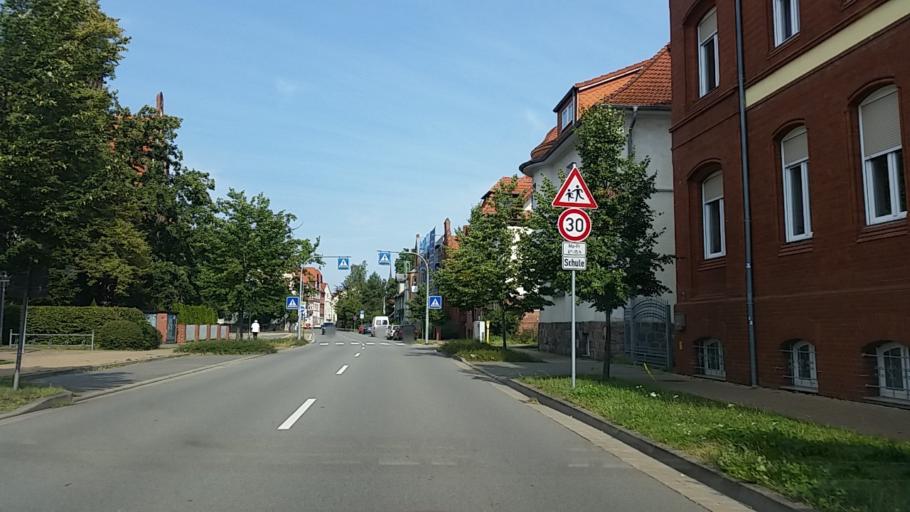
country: DE
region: Saxony-Anhalt
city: Salzwedel
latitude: 52.8463
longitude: 11.1517
